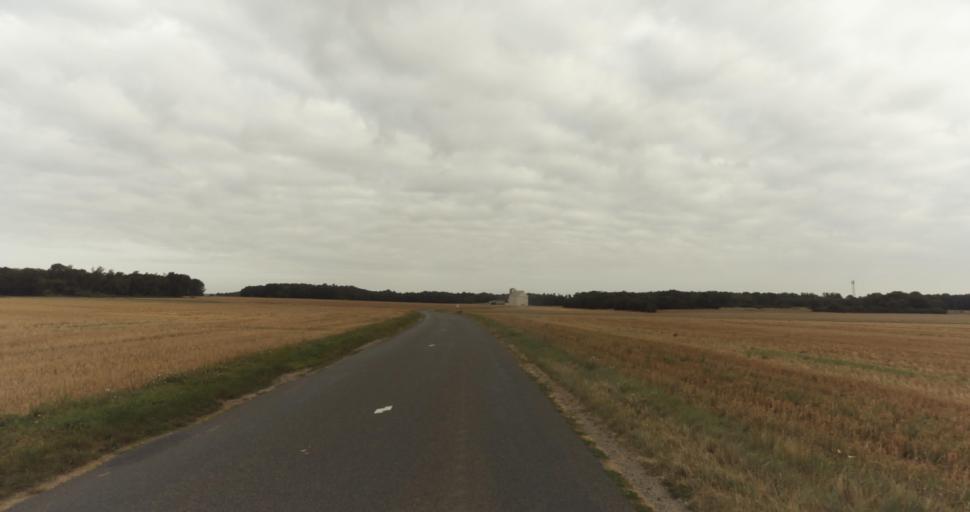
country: FR
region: Haute-Normandie
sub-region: Departement de l'Eure
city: Saint-Germain-sur-Avre
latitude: 48.7934
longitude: 1.2822
